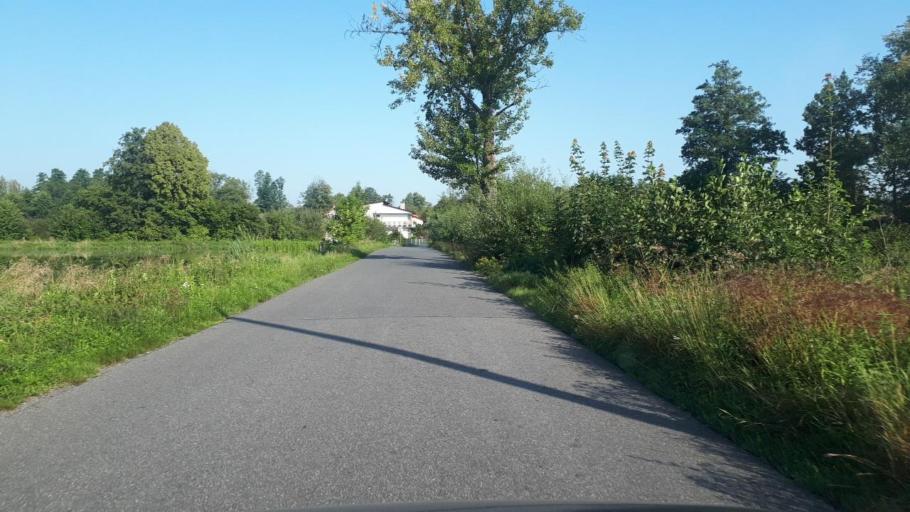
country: PL
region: Silesian Voivodeship
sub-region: Powiat cieszynski
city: Chybie
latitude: 49.8660
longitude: 18.8601
